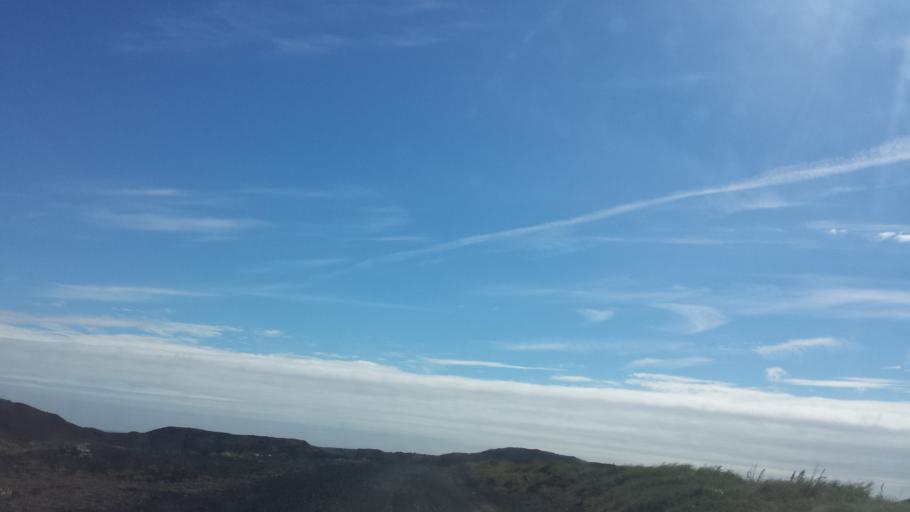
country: IS
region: South
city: Vestmannaeyjar
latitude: 63.4392
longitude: -20.2415
